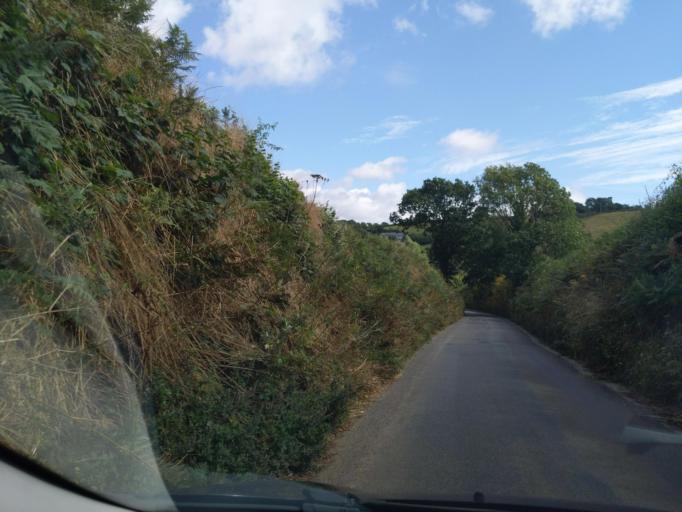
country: GB
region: England
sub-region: Devon
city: Modbury
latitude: 50.3591
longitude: -3.8933
